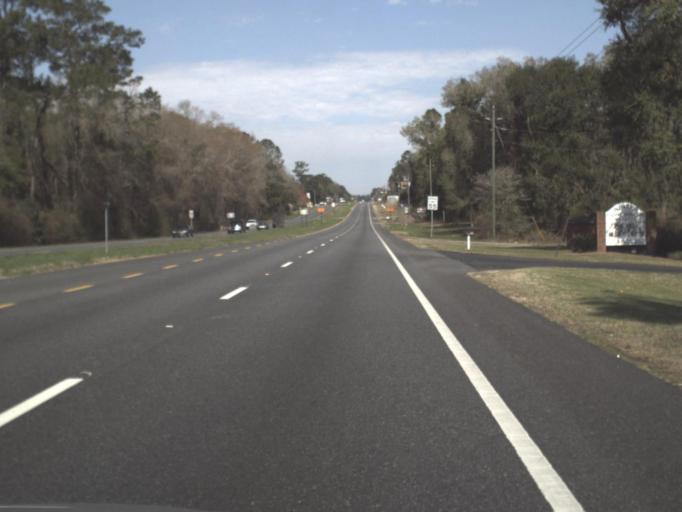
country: US
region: Florida
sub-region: Gadsden County
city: Havana
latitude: 30.5678
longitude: -84.3925
